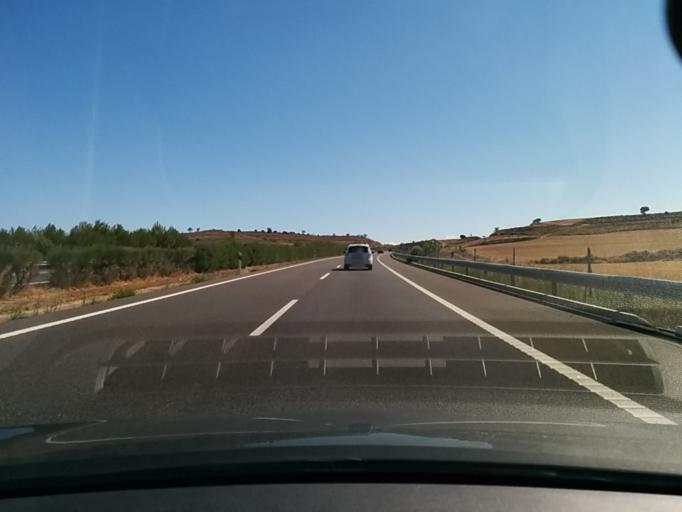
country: ES
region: Aragon
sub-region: Provincia de Huesca
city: Almudebar
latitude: 42.0561
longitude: -0.5423
